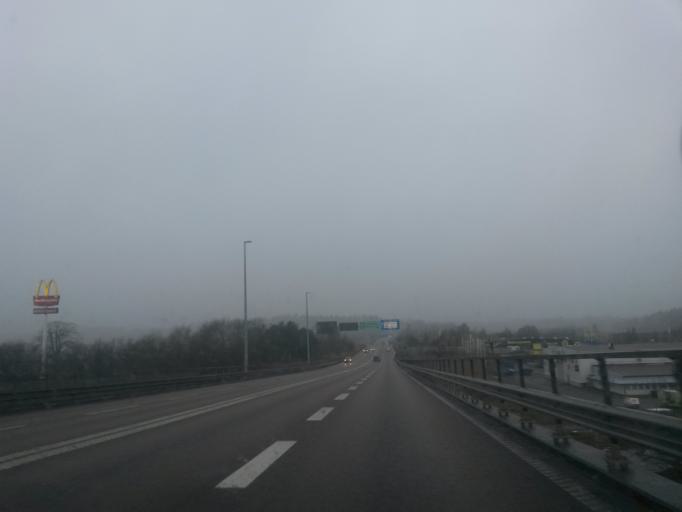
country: SE
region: Vaestra Goetaland
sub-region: Trollhattan
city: Trollhattan
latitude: 58.3140
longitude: 12.3110
